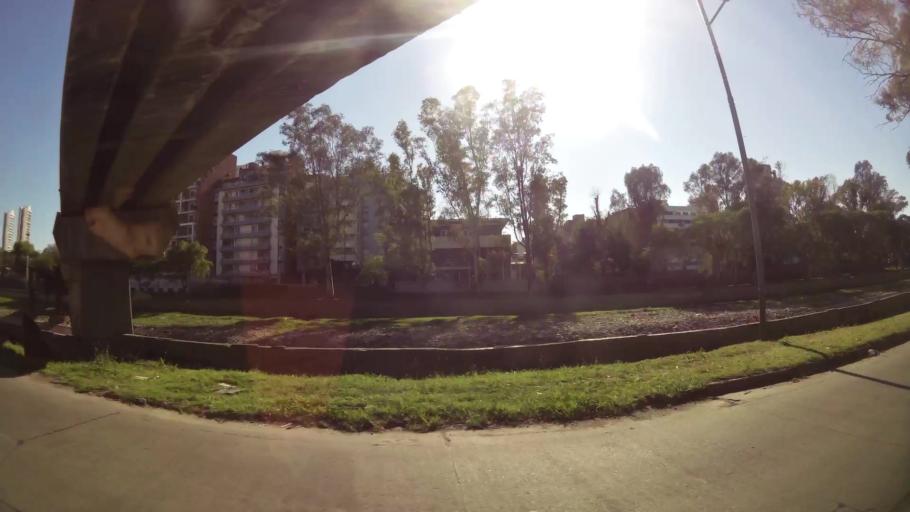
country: AR
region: Cordoba
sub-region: Departamento de Capital
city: Cordoba
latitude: -31.4147
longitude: -64.1748
